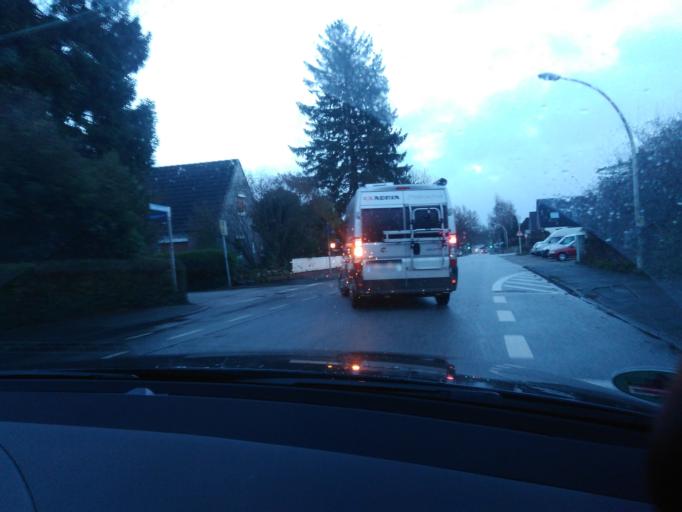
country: DE
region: Schleswig-Holstein
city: Altenholz
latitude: 54.3955
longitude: 10.1620
